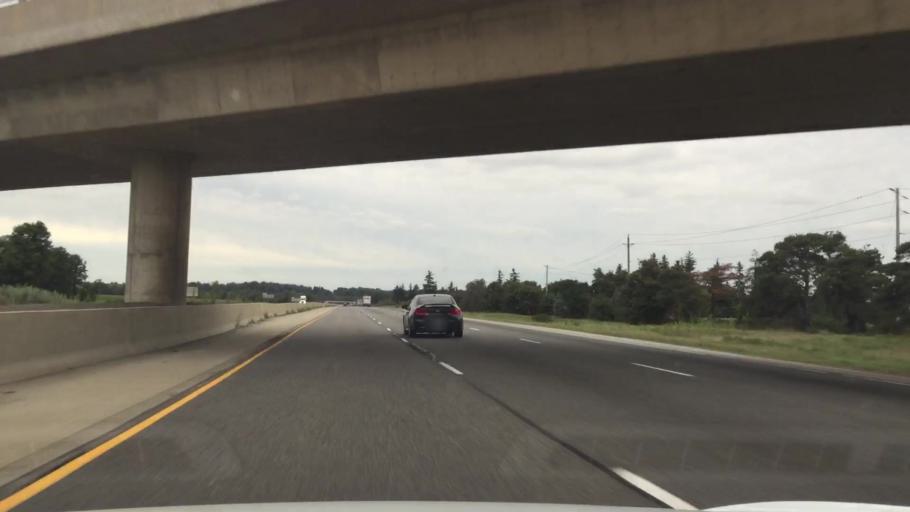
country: CA
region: Ontario
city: Kitchener
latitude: 43.3129
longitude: -80.4737
